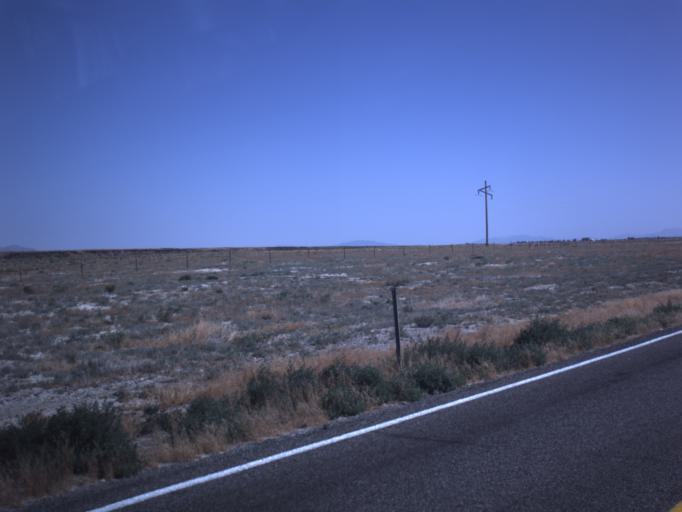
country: US
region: Utah
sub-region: Millard County
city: Delta
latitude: 39.1896
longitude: -112.6946
